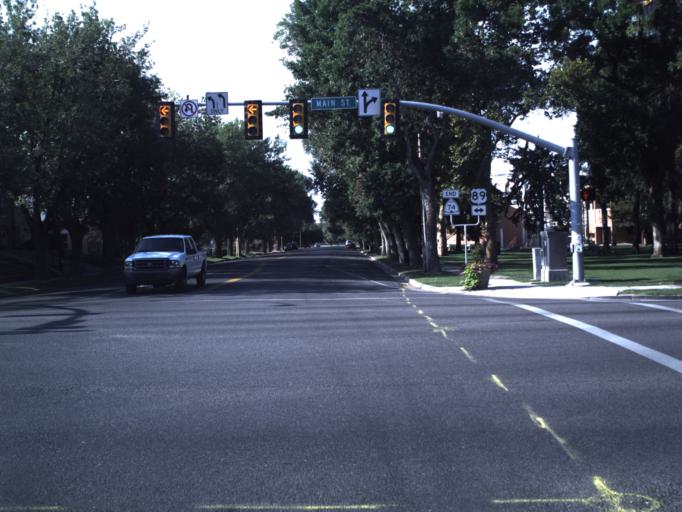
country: US
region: Utah
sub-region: Utah County
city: American Fork
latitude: 40.3769
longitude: -111.7960
